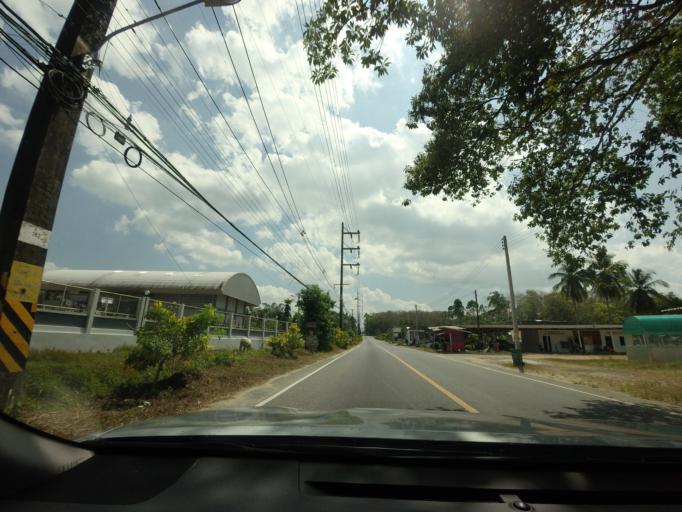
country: TH
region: Phangnga
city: Thai Mueang
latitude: 8.3968
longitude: 98.2611
